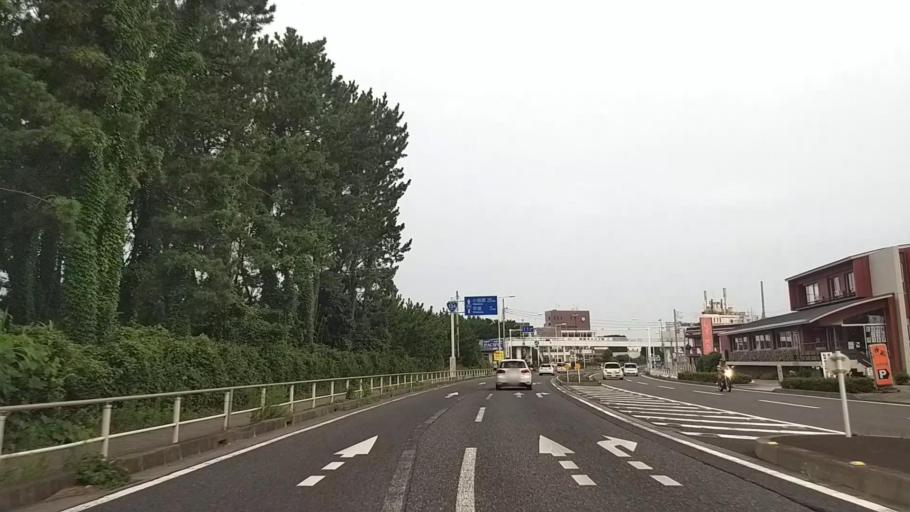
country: JP
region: Kanagawa
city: Chigasaki
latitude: 35.3169
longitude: 139.3839
